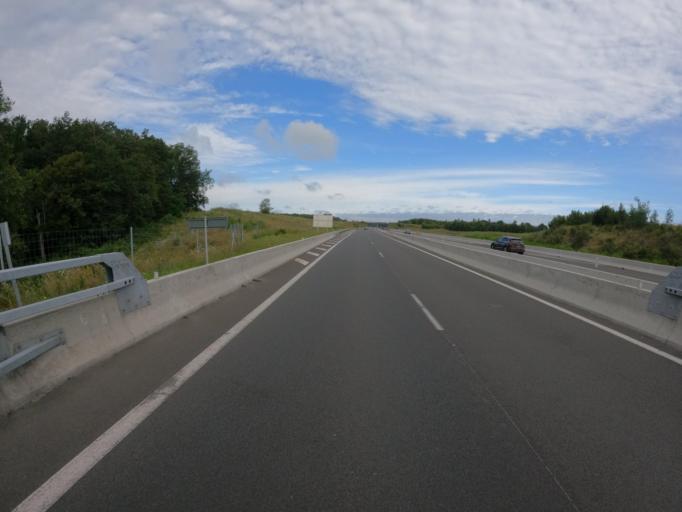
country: FR
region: Centre
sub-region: Departement d'Indre-et-Loire
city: Cinq-Mars-la-Pile
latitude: 47.3374
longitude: 0.4310
